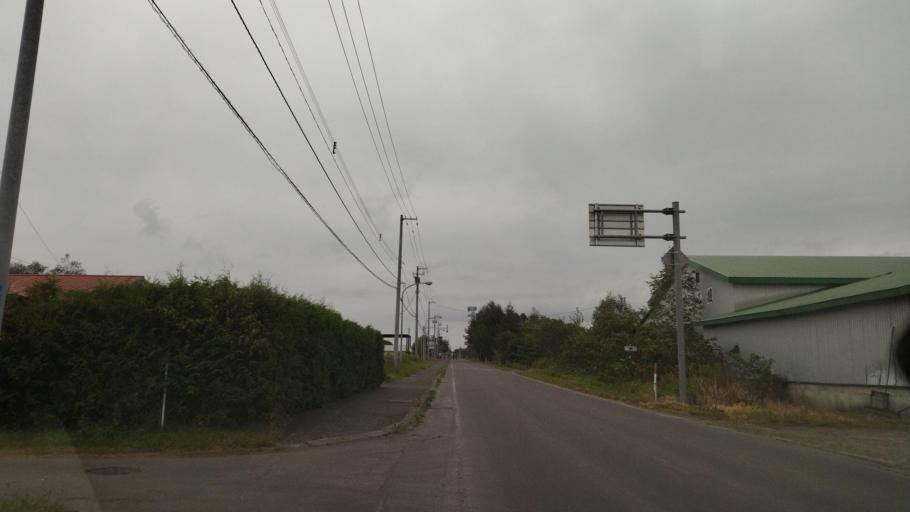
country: JP
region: Hokkaido
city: Otofuke
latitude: 43.2265
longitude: 143.2804
